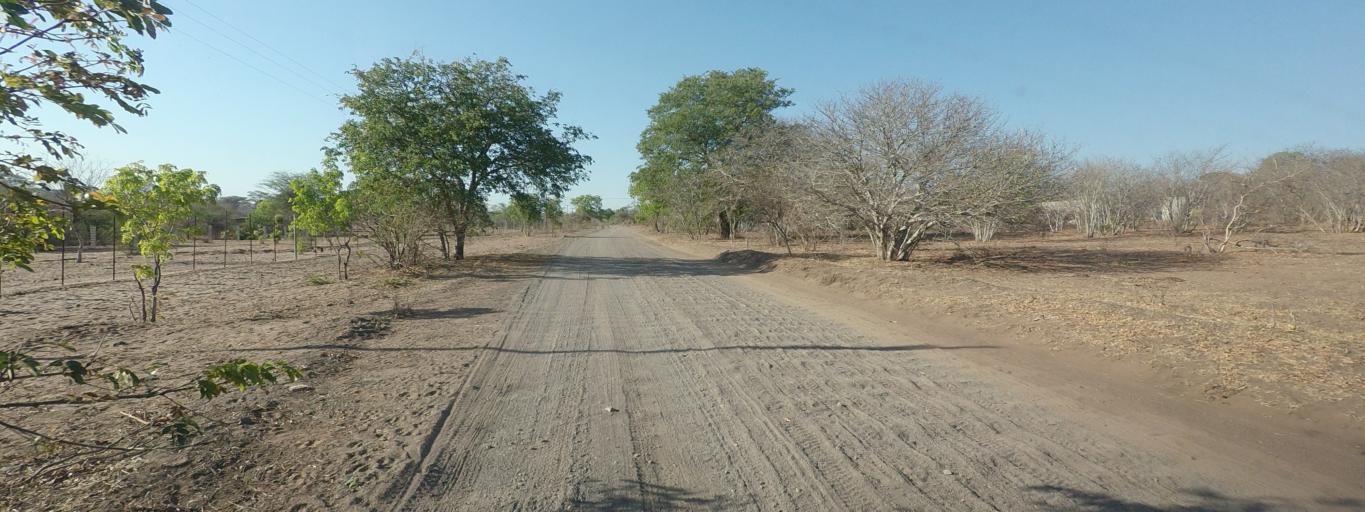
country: BW
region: North West
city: Kasane
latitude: -17.8912
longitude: 25.2293
